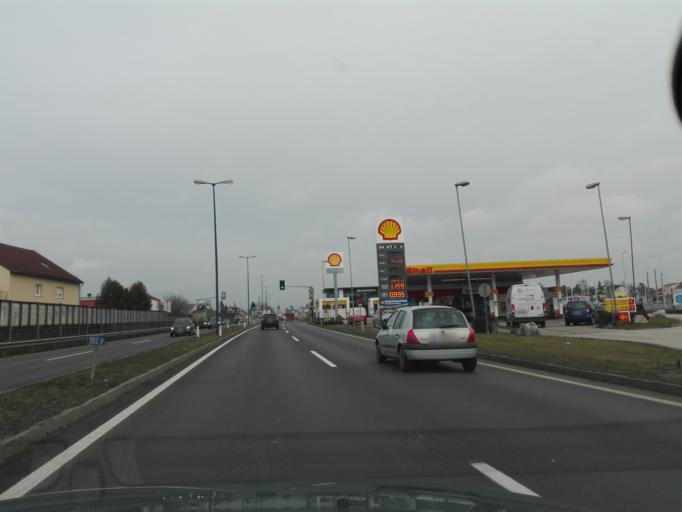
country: AT
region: Upper Austria
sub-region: Politischer Bezirk Linz-Land
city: Traun
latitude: 48.2338
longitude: 14.2314
